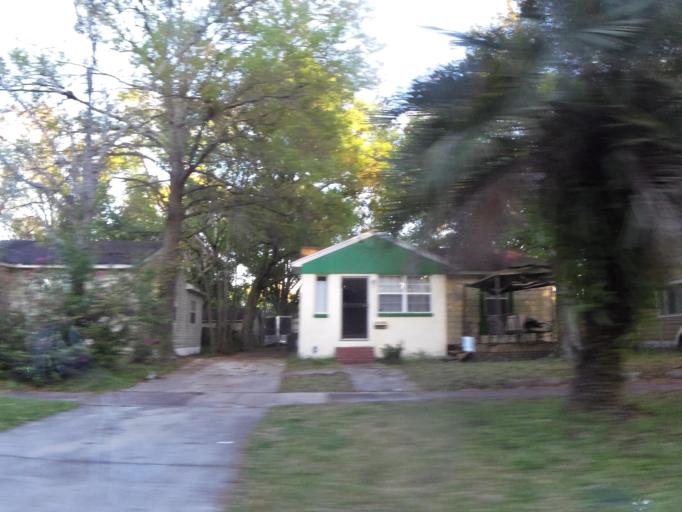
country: US
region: Florida
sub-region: Duval County
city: Jacksonville
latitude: 30.3362
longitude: -81.7130
